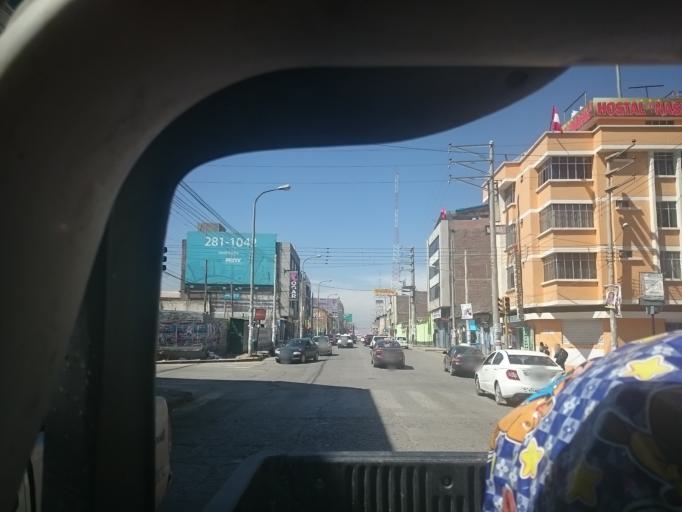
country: PE
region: Junin
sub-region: Provincia de Huancayo
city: El Tambo
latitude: -12.0601
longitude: -75.2155
